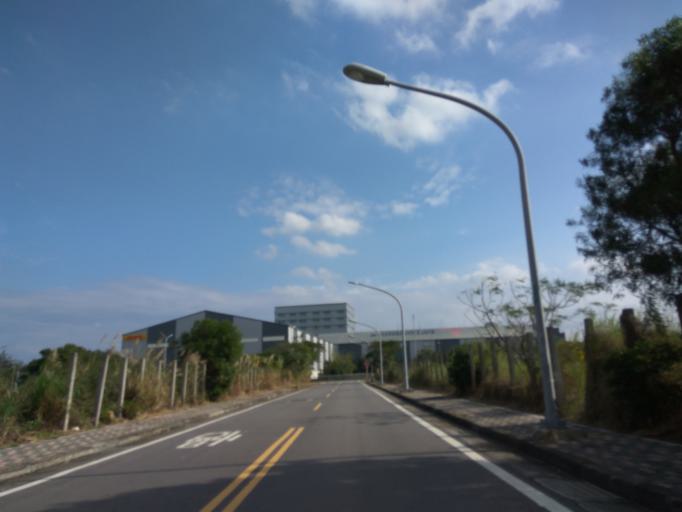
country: TW
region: Taiwan
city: Taoyuan City
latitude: 25.0502
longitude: 121.1747
